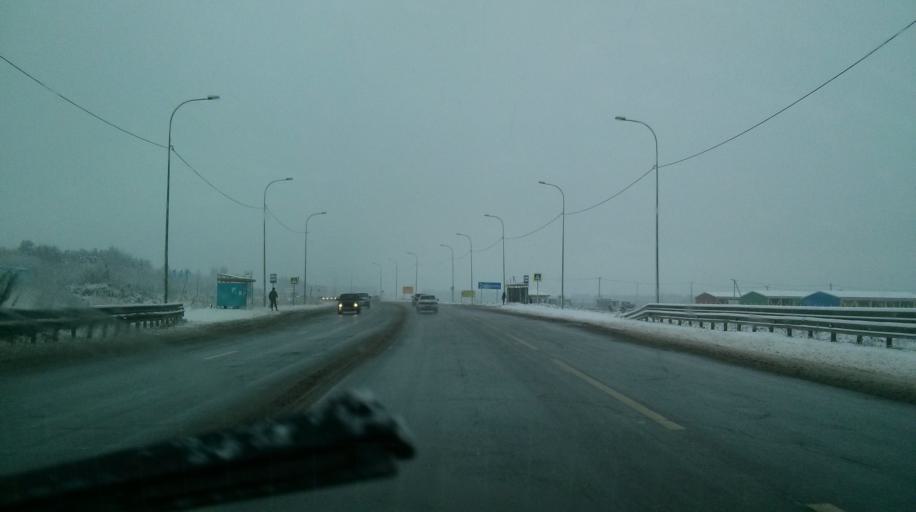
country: RU
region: Nizjnij Novgorod
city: Burevestnik
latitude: 56.1696
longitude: 43.7376
